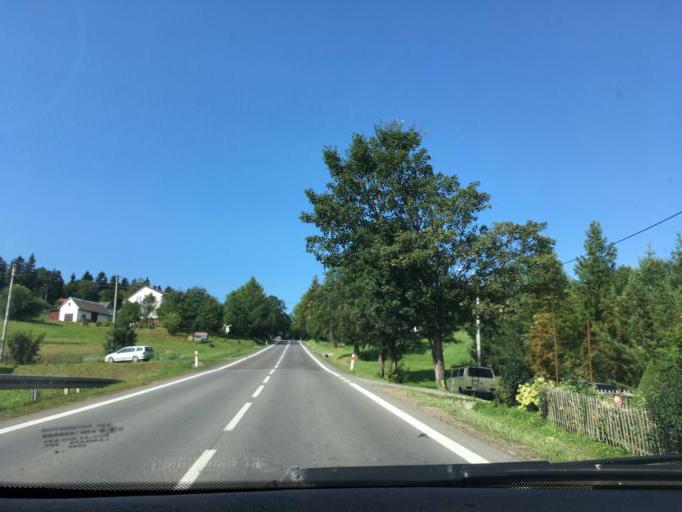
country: PL
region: Subcarpathian Voivodeship
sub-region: Powiat leski
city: Uherce Mineralne
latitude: 49.4660
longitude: 22.3711
